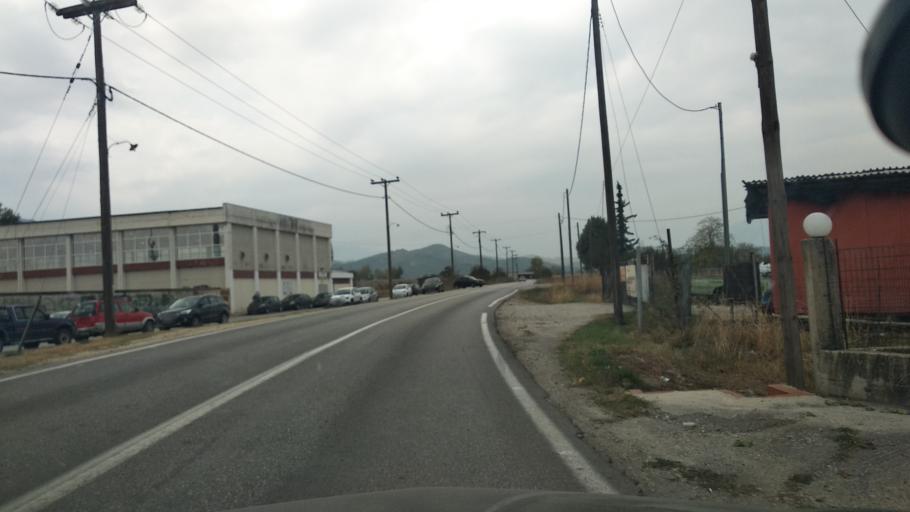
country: GR
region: Thessaly
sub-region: Trikala
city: Kalampaka
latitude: 39.7016
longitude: 21.6127
